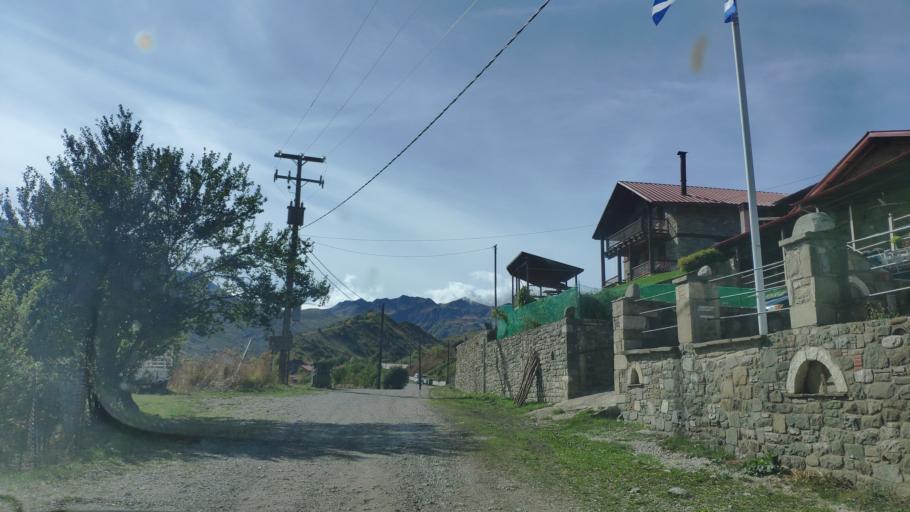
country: AL
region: Korce
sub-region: Rrethi i Devollit
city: Miras
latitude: 40.3937
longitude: 20.8363
